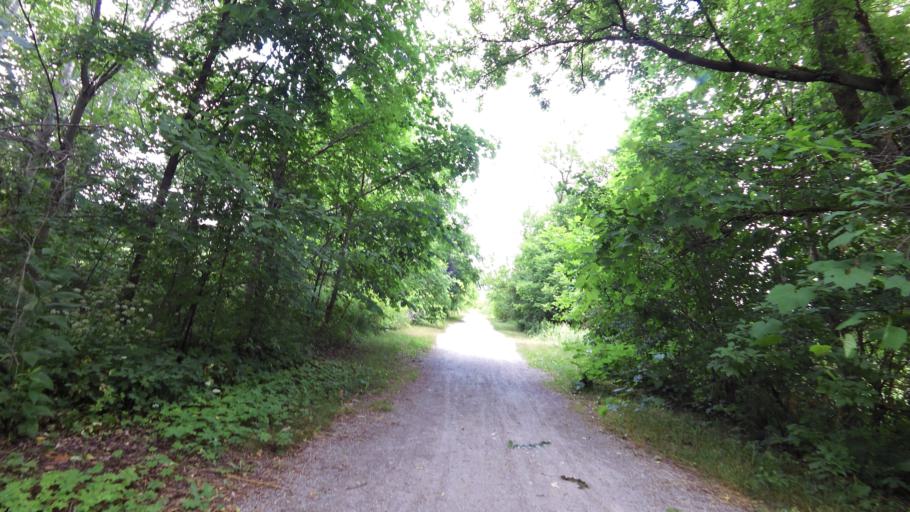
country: CA
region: Ontario
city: Brampton
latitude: 43.7970
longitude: -79.9317
